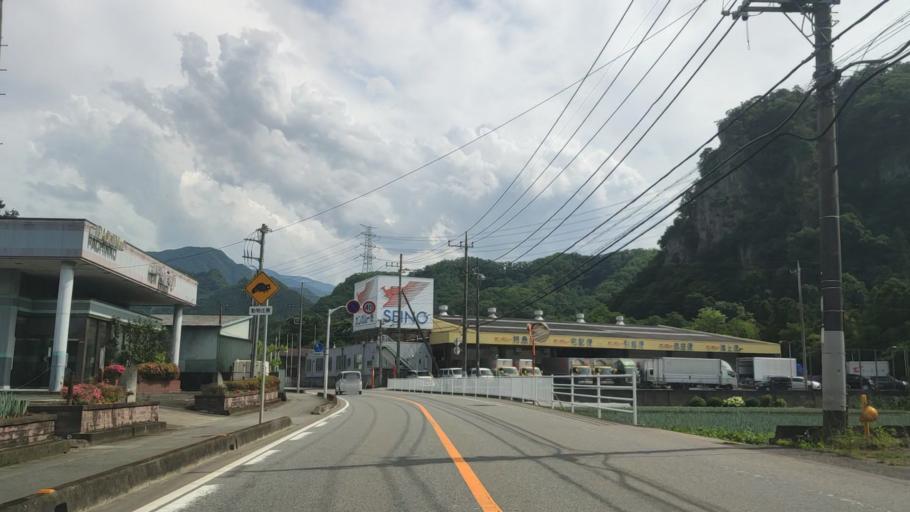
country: JP
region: Gunma
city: Tomioka
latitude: 36.2206
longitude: 138.7991
